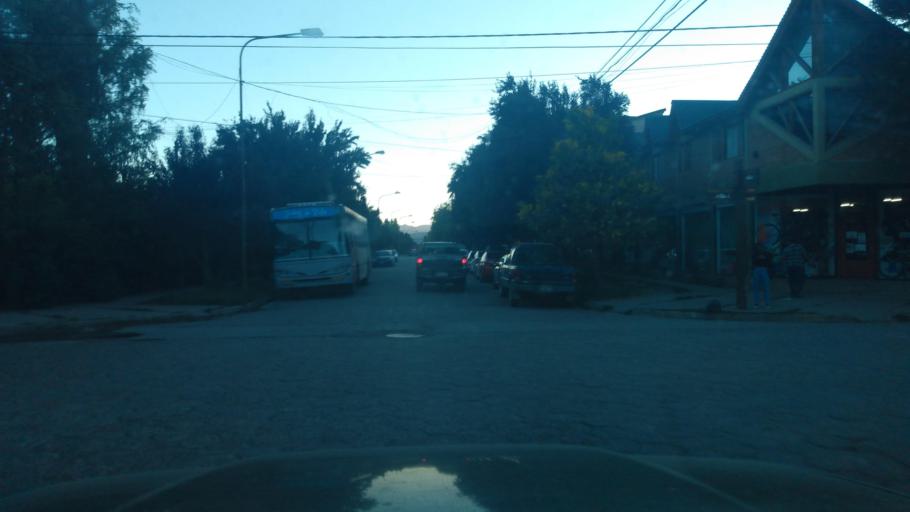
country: AR
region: Neuquen
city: Junin de los Andes
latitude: -39.9517
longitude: -71.0748
